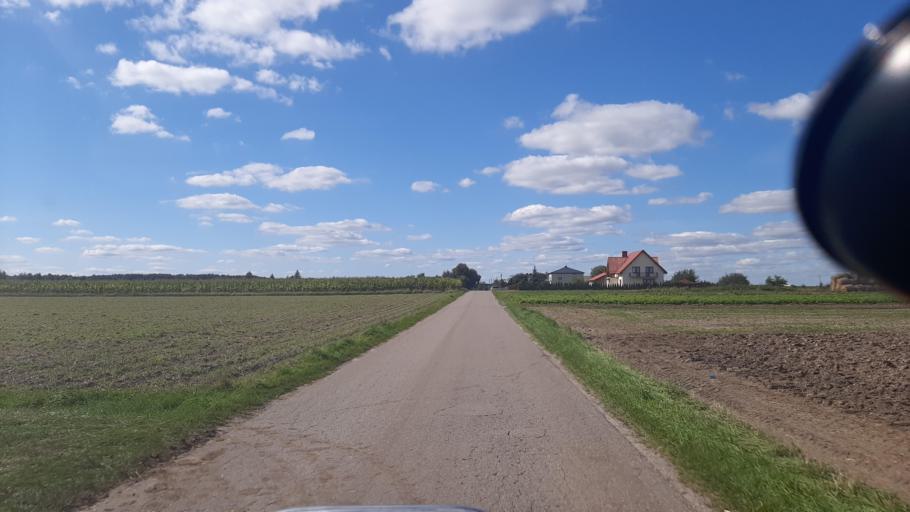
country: PL
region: Lublin Voivodeship
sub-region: Powiat lubartowski
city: Kamionka
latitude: 51.4053
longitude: 22.4059
